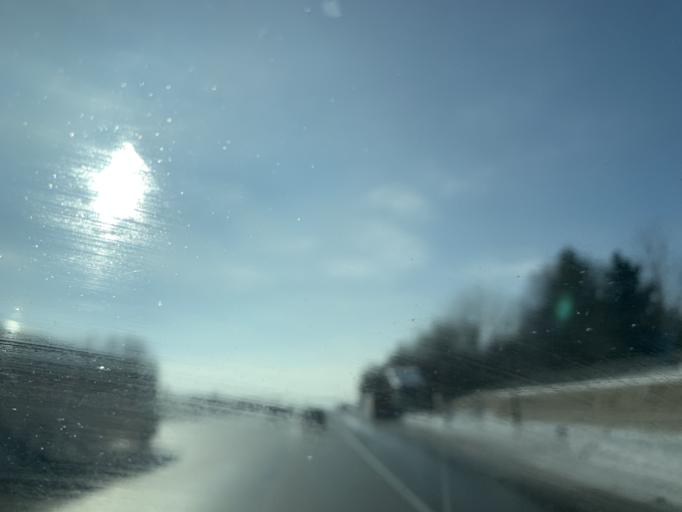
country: US
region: Minnesota
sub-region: Dakota County
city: Apple Valley
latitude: 44.7492
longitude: -93.2179
